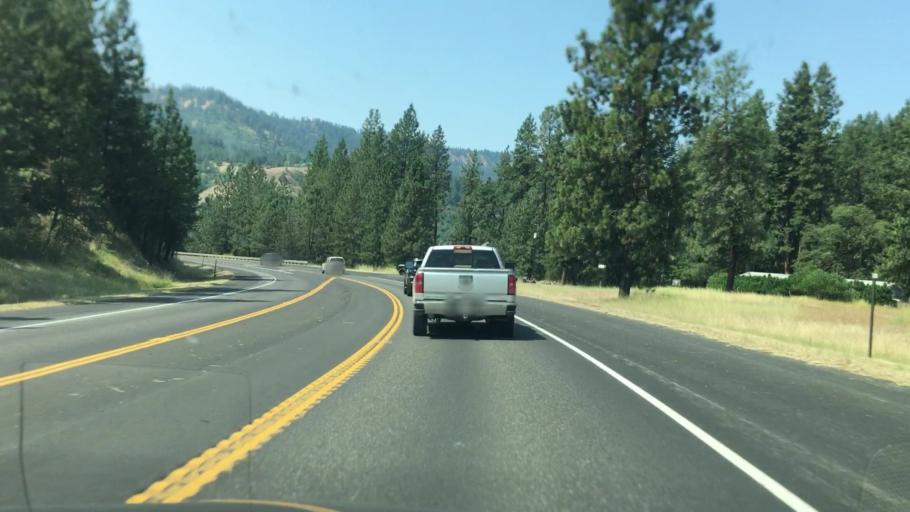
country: US
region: Idaho
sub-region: Nez Perce County
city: Lapwai
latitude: 46.5103
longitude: -116.5605
